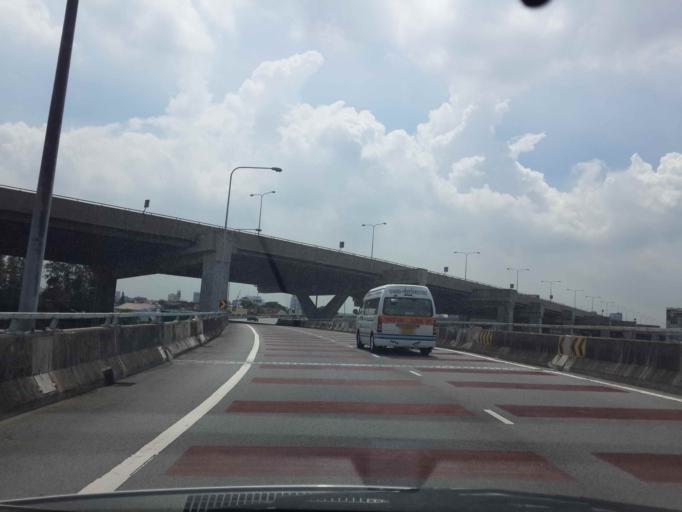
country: TH
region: Bangkok
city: Phra Khanong
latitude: 13.6980
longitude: 100.5912
